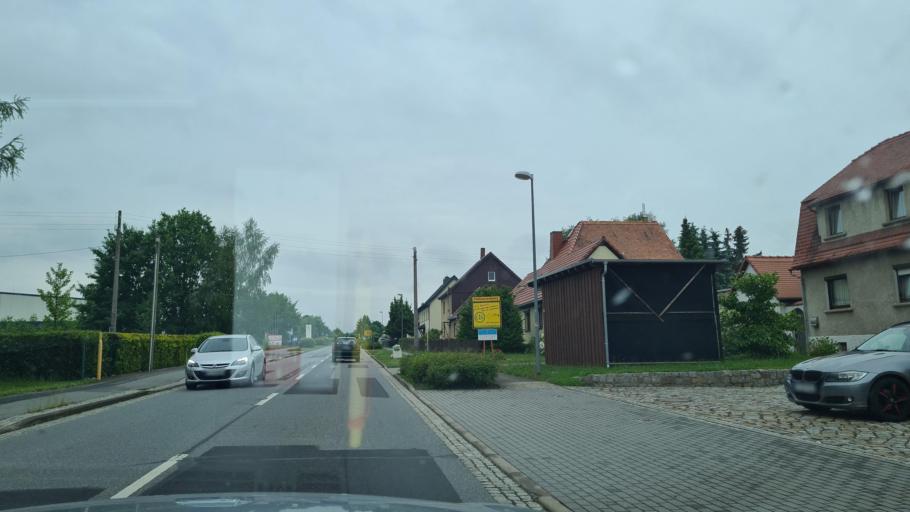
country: DE
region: Saxony
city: Schirgiswalde
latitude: 51.0586
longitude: 14.4299
